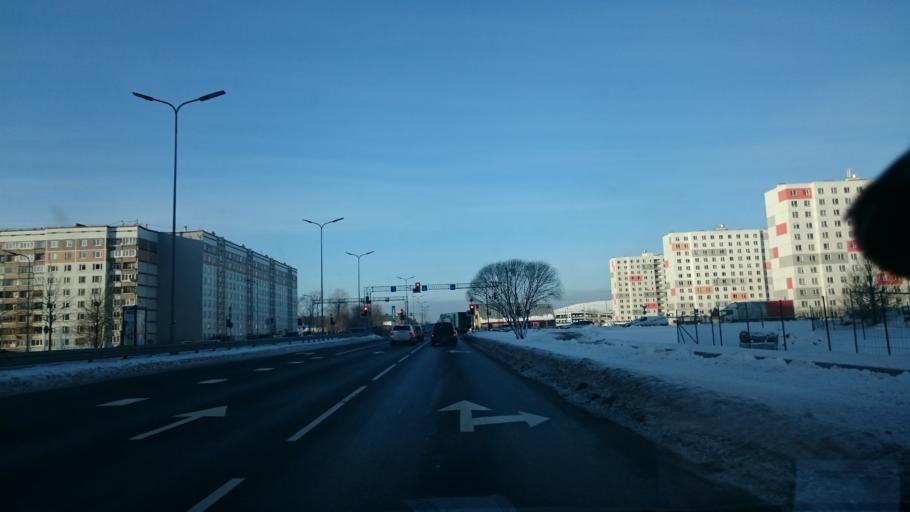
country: LV
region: Stopini
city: Ulbroka
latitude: 56.9448
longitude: 24.2192
